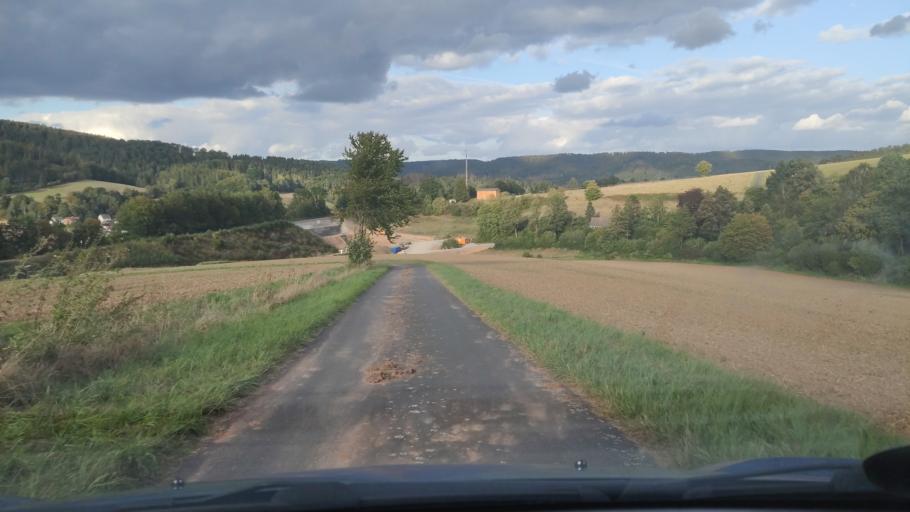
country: DE
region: Lower Saxony
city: Uslar
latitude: 51.6564
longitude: 9.7107
